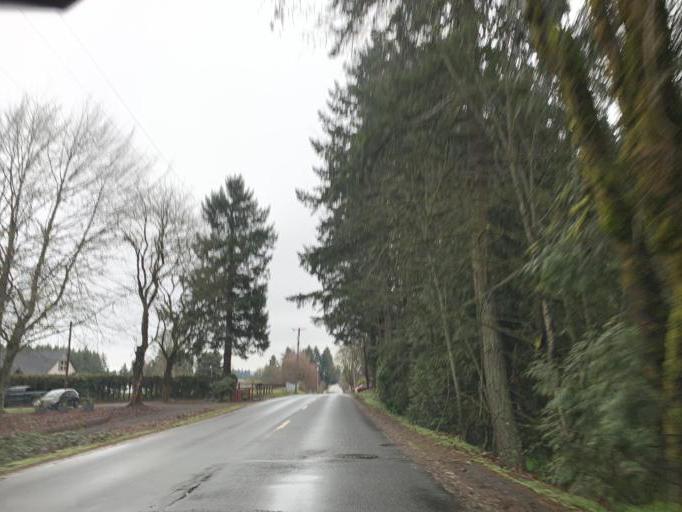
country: US
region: Washington
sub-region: Clark County
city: Five Corners
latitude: 45.6861
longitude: -122.5866
